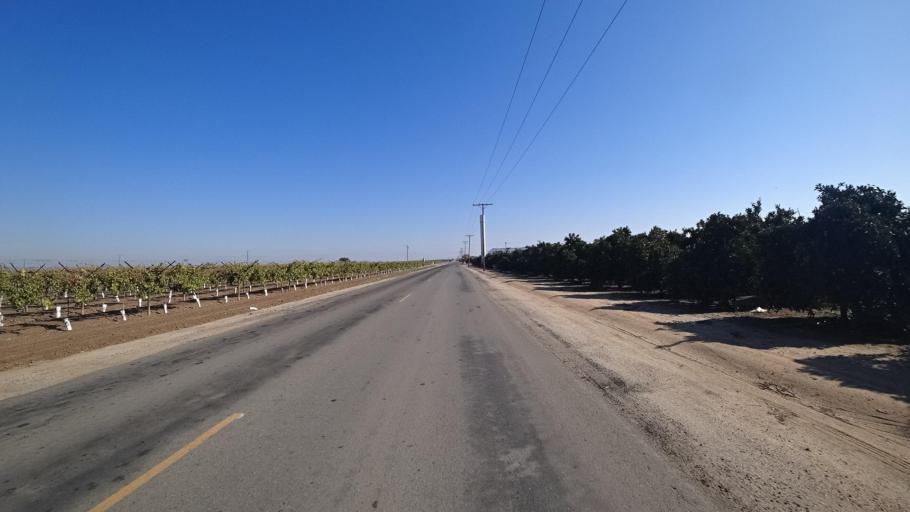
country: US
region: California
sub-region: Kern County
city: McFarland
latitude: 35.7180
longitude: -119.1537
